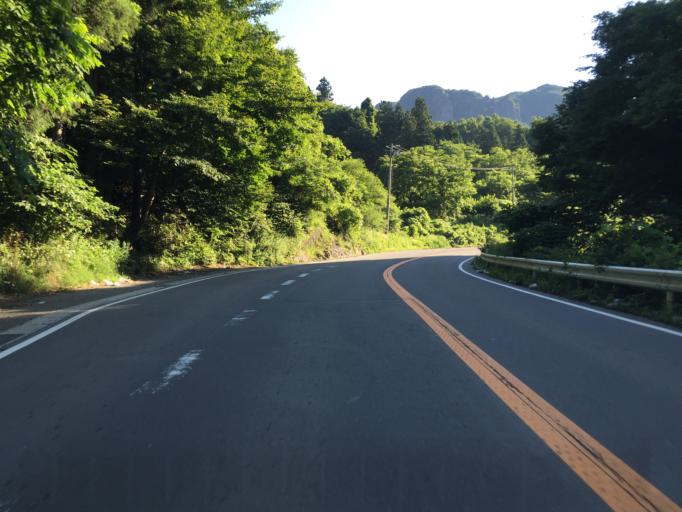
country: JP
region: Fukushima
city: Yanagawamachi-saiwaicho
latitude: 37.7553
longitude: 140.6763
